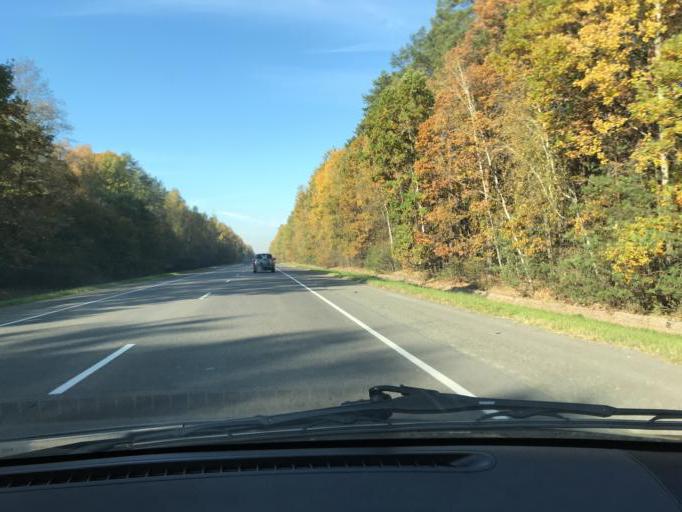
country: BY
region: Brest
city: Horad Luninyets
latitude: 52.2942
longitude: 26.7558
